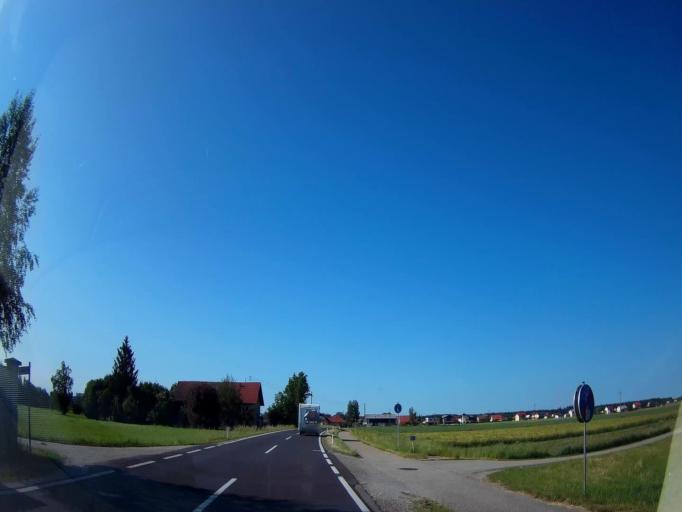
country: AT
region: Upper Austria
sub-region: Politischer Bezirk Braunau am Inn
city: Braunau am Inn
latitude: 48.1721
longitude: 13.0495
